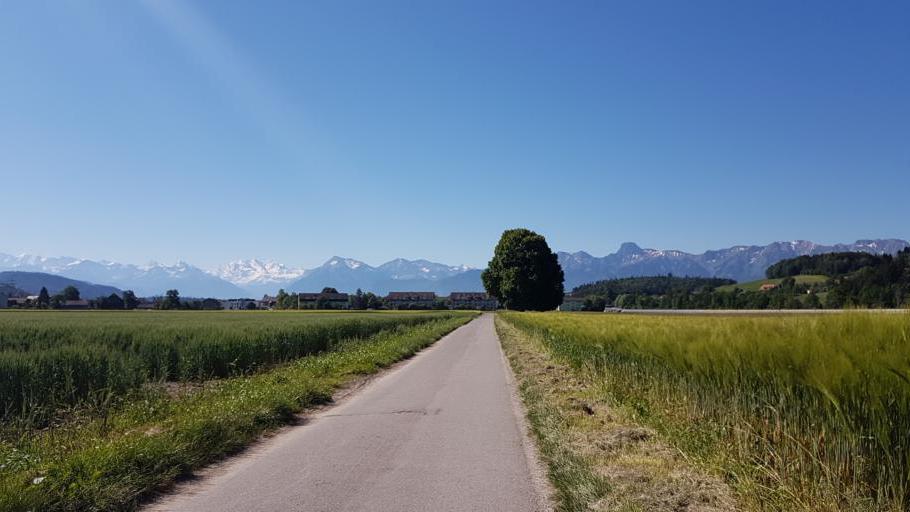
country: CH
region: Bern
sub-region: Bern-Mittelland District
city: Niederwichtrach
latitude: 46.8439
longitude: 7.5626
